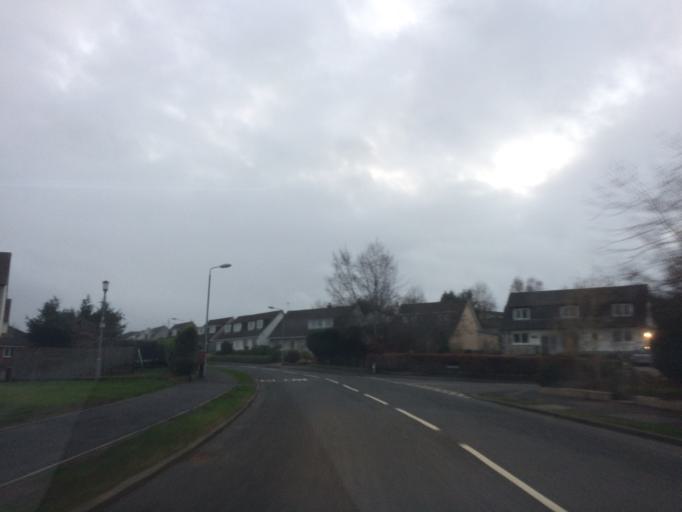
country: GB
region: Scotland
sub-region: East Renfrewshire
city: Newton Mearns
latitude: 55.7838
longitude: -4.3336
